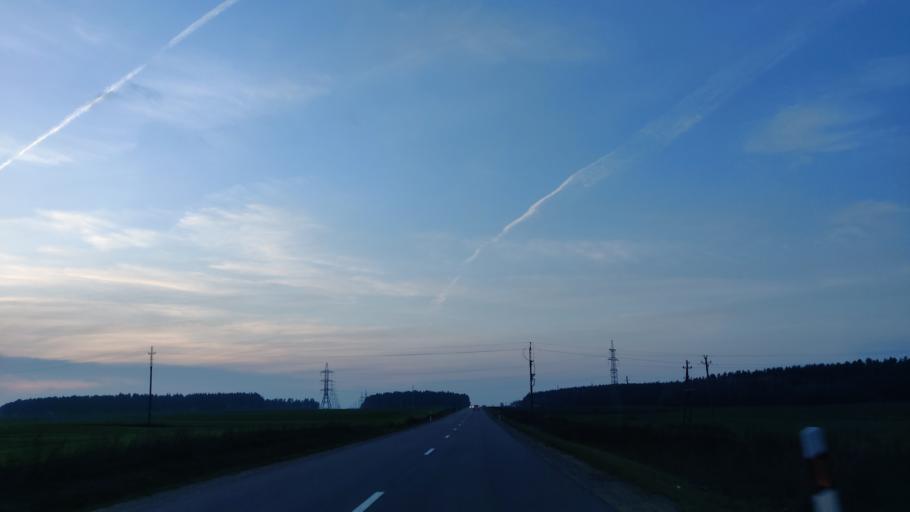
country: LT
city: Lentvaris
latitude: 54.5942
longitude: 25.0412
